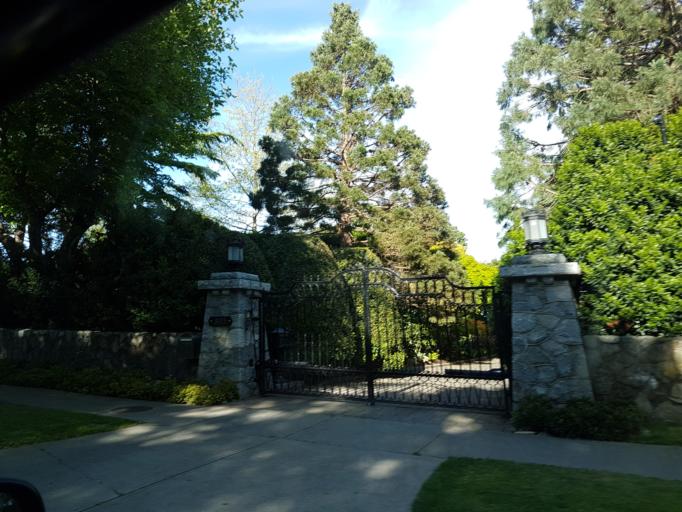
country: CA
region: British Columbia
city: Oak Bay
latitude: 48.4440
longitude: -123.2933
